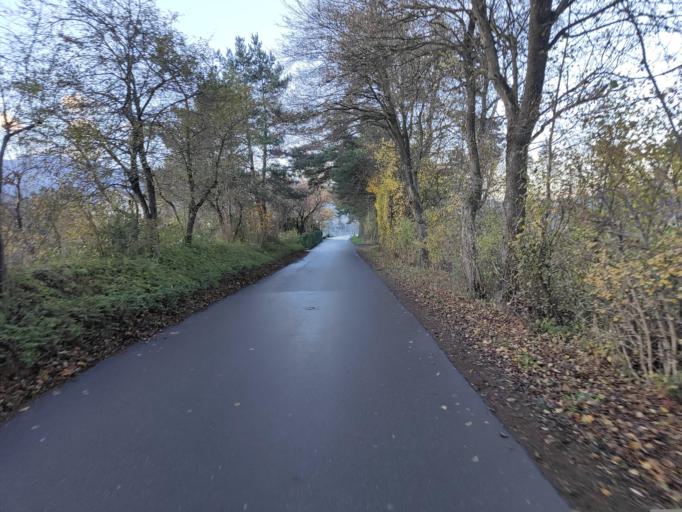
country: LI
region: Eschen
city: Eschen
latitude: 47.1913
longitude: 9.5246
